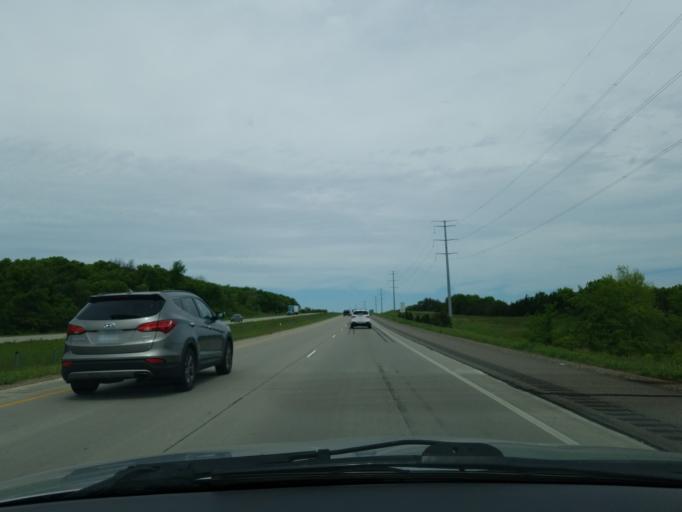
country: US
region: Minnesota
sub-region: Stearns County
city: Saint Augusta
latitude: 45.4709
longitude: -94.1347
